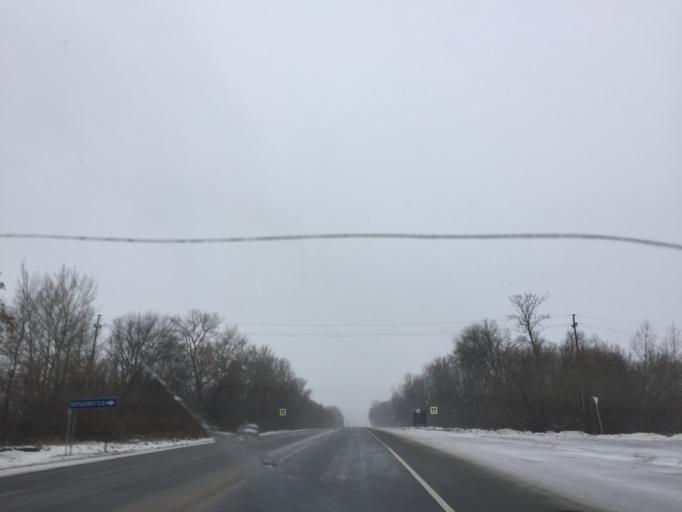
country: RU
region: Tula
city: Plavsk
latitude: 53.7328
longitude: 37.3092
